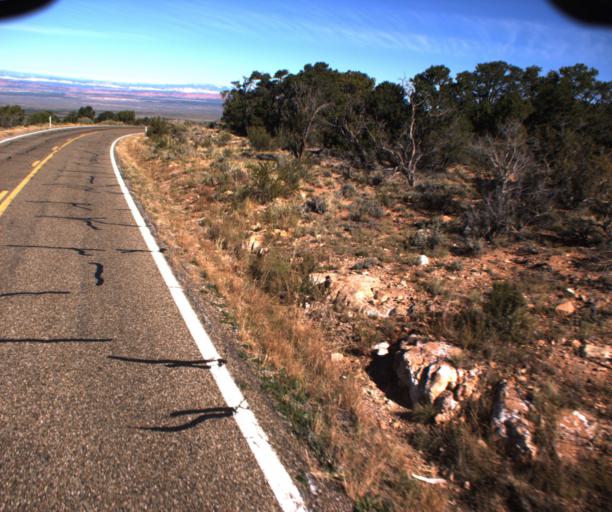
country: US
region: Arizona
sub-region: Coconino County
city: Fredonia
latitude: 36.8378
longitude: -112.2554
